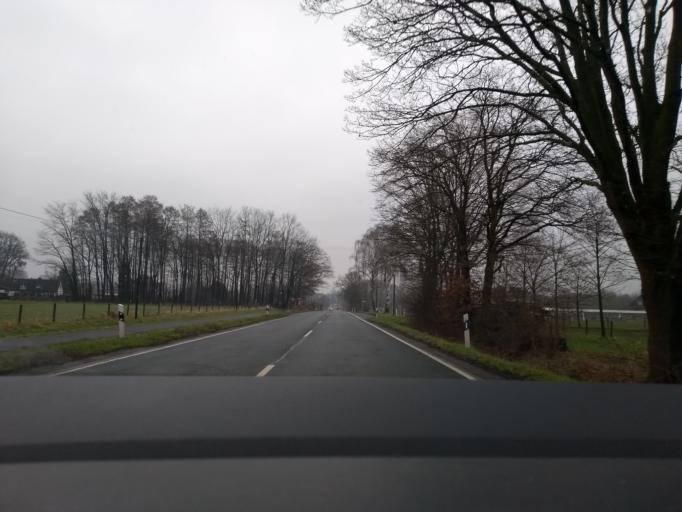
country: DE
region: North Rhine-Westphalia
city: Waltrop
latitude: 51.6423
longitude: 7.4423
